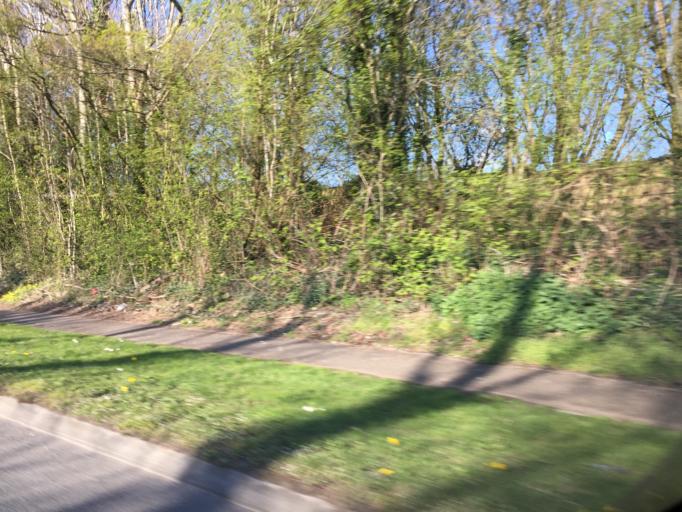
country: GB
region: Wales
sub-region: Torfaen County Borough
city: Cwmbran
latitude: 51.6404
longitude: -3.0214
